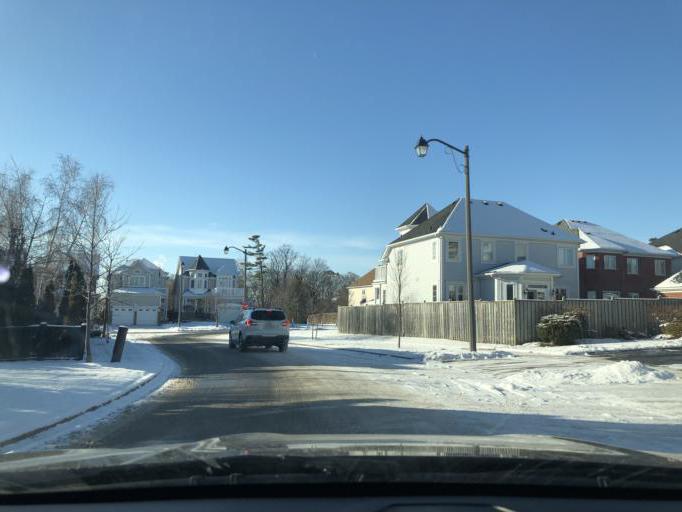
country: CA
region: Ontario
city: Scarborough
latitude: 43.7730
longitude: -79.1403
